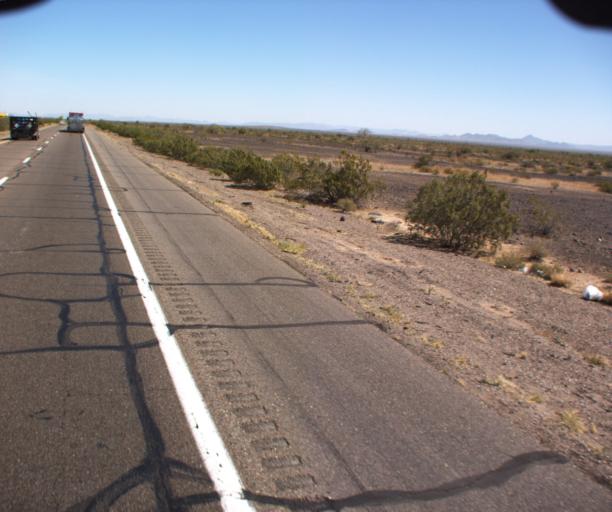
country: US
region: Arizona
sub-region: Maricopa County
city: Gila Bend
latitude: 32.8917
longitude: -113.0506
